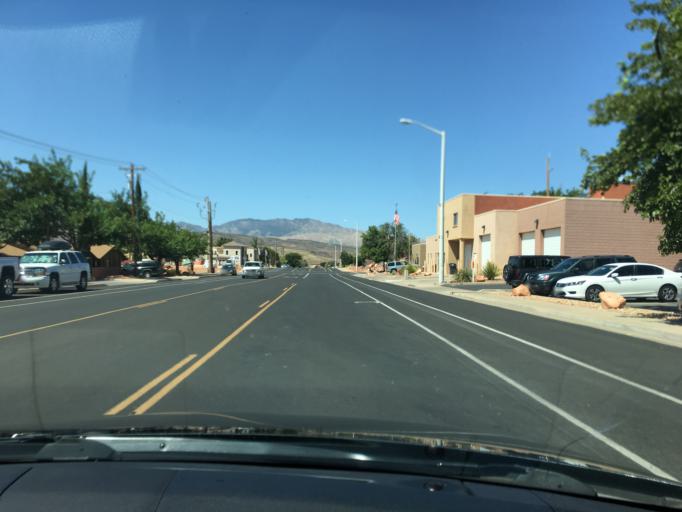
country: US
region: Utah
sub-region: Washington County
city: Ivins
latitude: 37.1683
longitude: -113.6807
